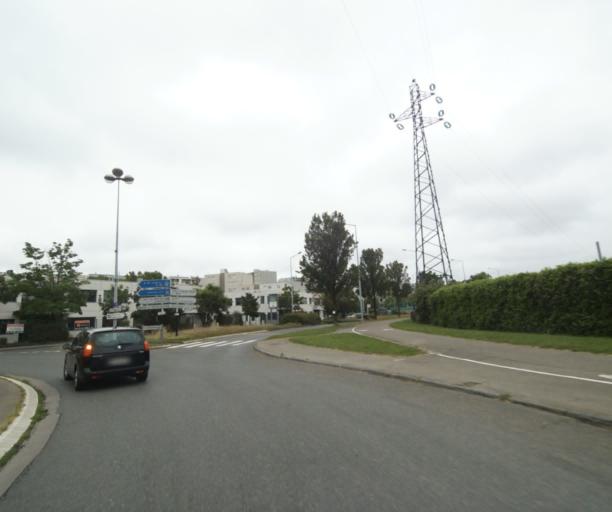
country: FR
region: Rhone-Alpes
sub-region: Departement du Rhone
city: Vaulx-en-Velin
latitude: 45.7884
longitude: 4.9068
